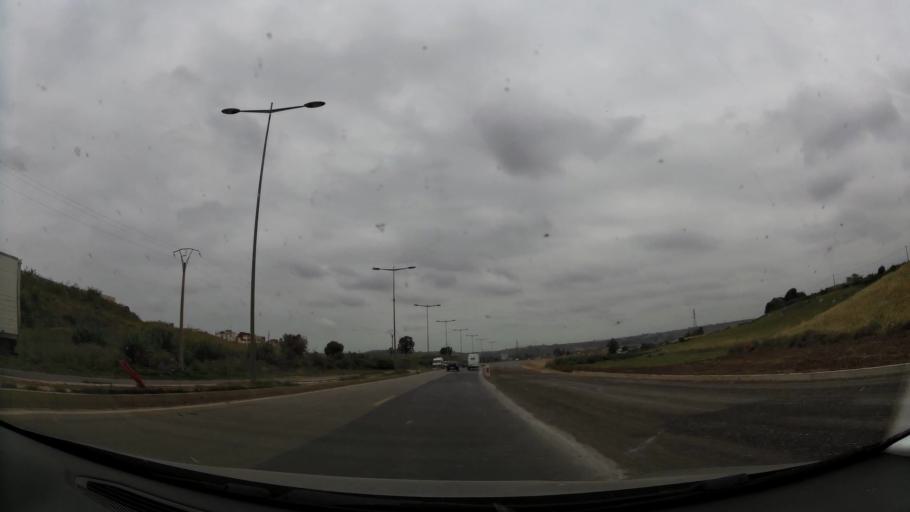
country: MA
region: Rabat-Sale-Zemmour-Zaer
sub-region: Rabat
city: Rabat
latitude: 33.9834
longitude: -6.8011
